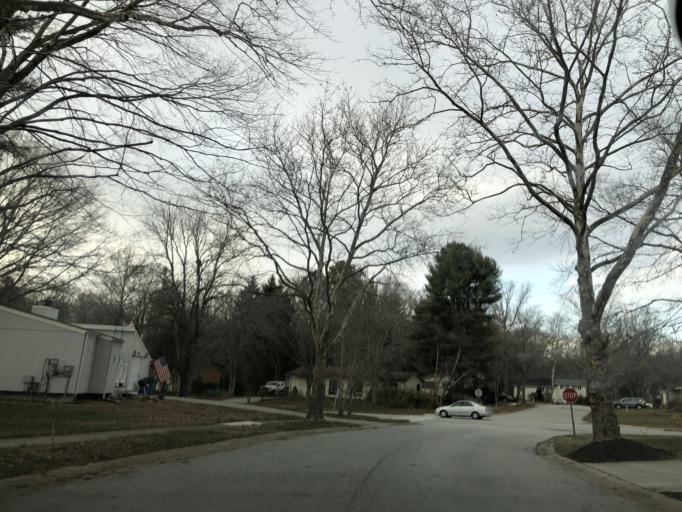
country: US
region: Maryland
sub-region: Howard County
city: Columbia
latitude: 39.2029
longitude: -76.8367
